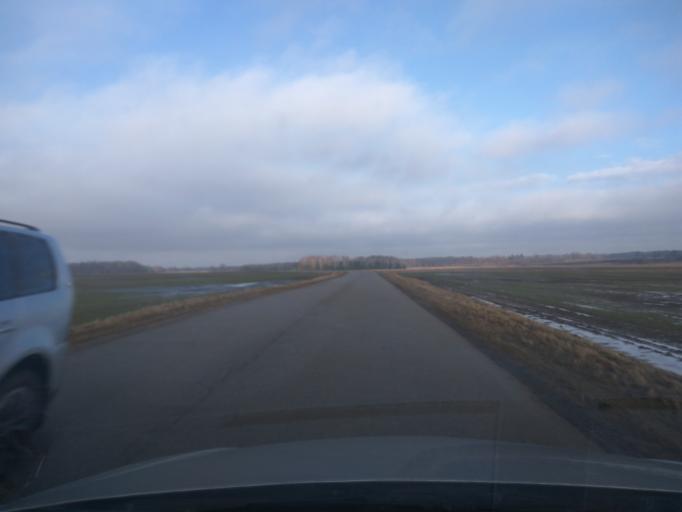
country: LV
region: Saldus Rajons
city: Saldus
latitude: 56.7494
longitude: 22.3858
